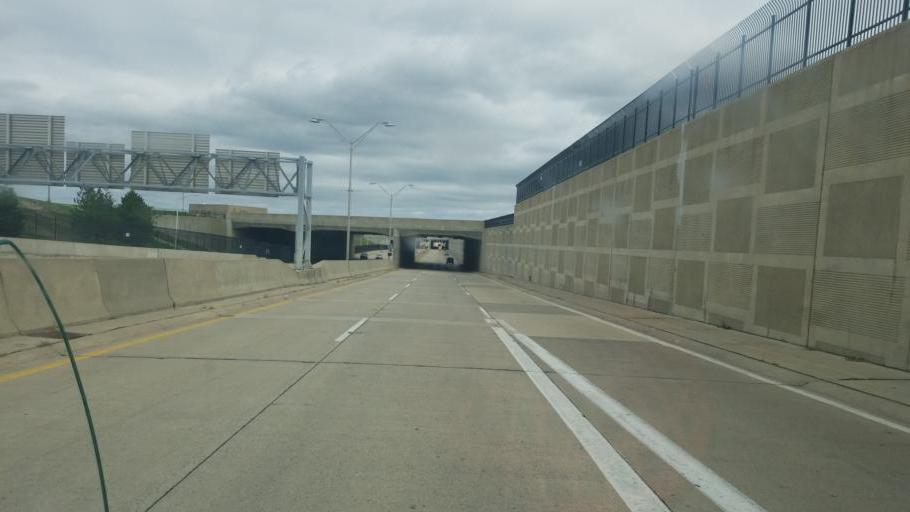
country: US
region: Michigan
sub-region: Wayne County
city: Romulus
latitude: 42.2123
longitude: -83.3506
